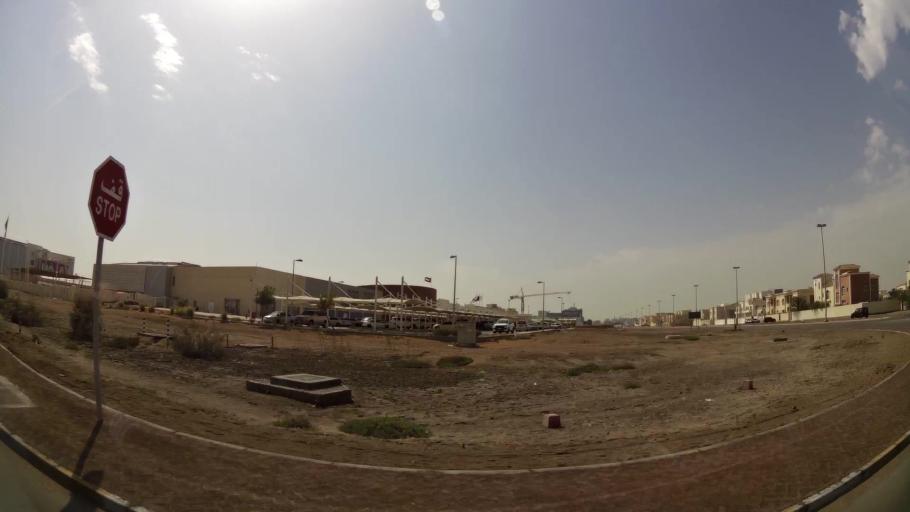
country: AE
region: Abu Dhabi
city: Abu Dhabi
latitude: 24.3184
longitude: 54.5618
